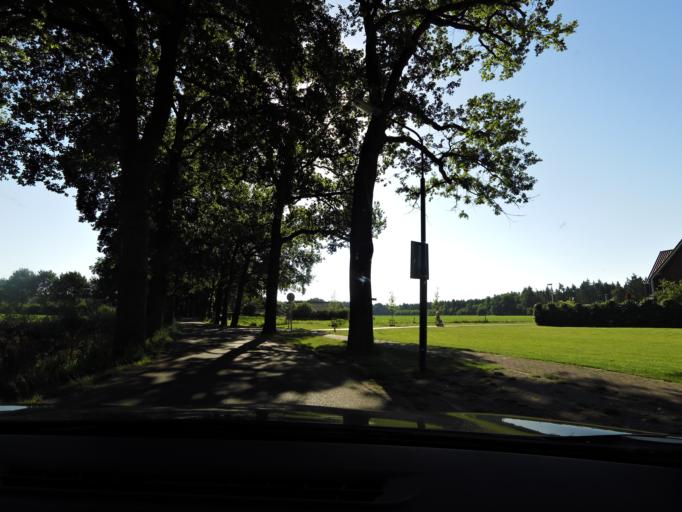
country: NL
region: Gelderland
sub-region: Gemeente Lochem
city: Harfsen
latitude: 52.2765
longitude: 6.2747
